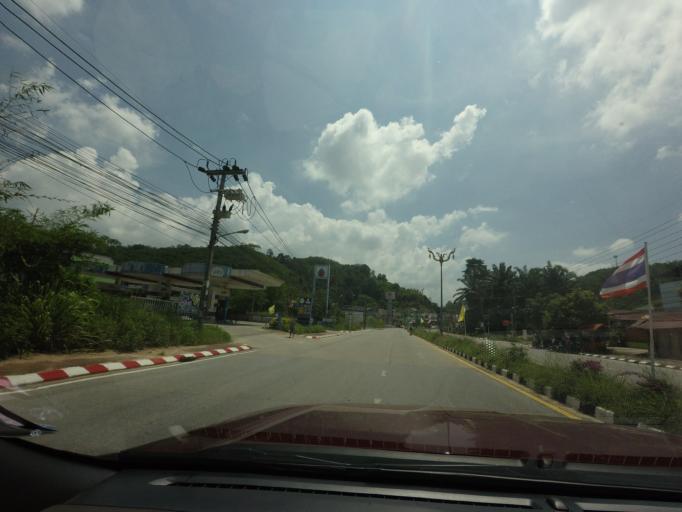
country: TH
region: Yala
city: Betong
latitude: 5.7871
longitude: 101.0722
